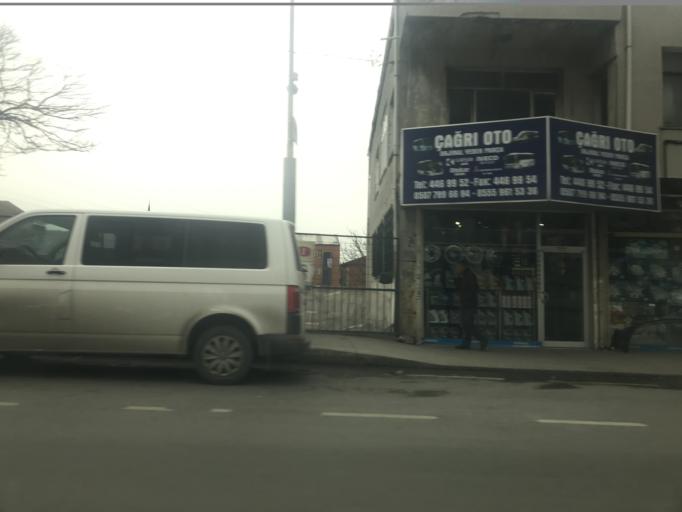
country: TR
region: Istanbul
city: Mahmutbey
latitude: 41.0457
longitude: 28.8303
